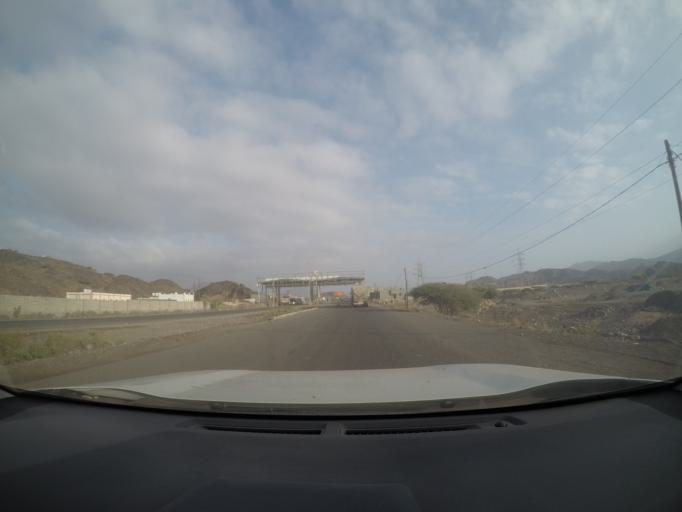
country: YE
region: Lahij
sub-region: Al Milah
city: Al Milah
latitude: 13.2839
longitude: 44.7564
